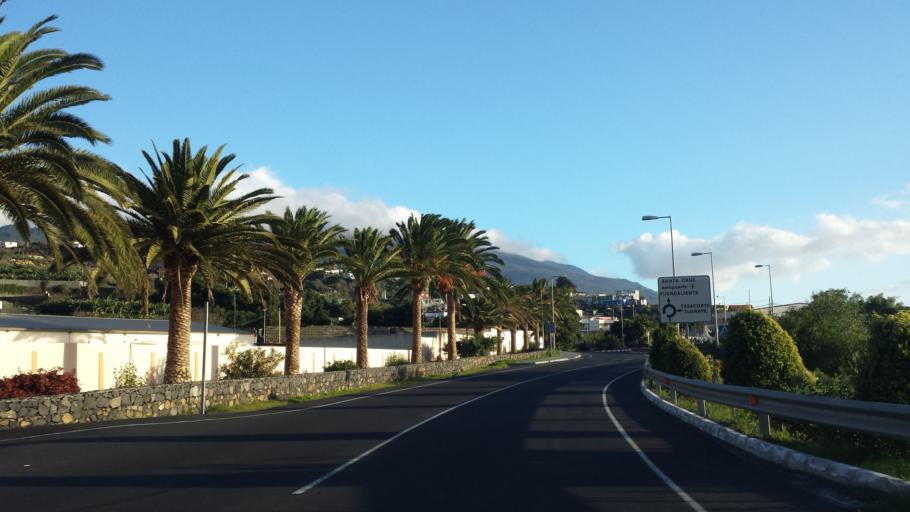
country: ES
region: Canary Islands
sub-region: Provincia de Santa Cruz de Tenerife
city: Los Llanos de Aridane
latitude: 28.6535
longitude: -17.9024
